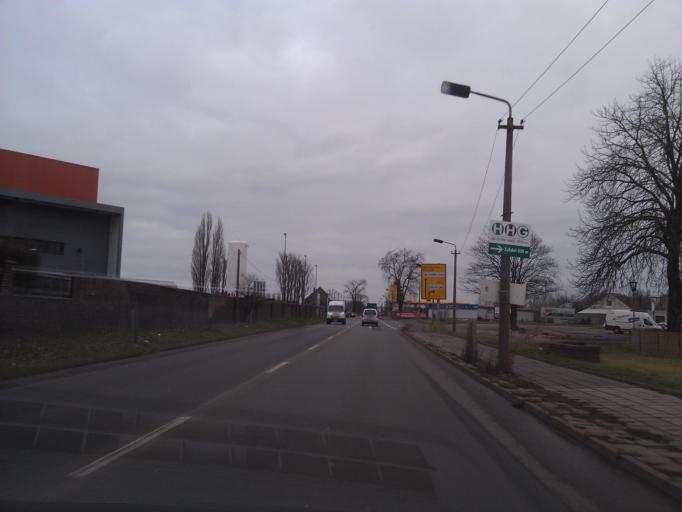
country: DE
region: Thuringia
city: Gotha
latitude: 50.9623
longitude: 10.7225
